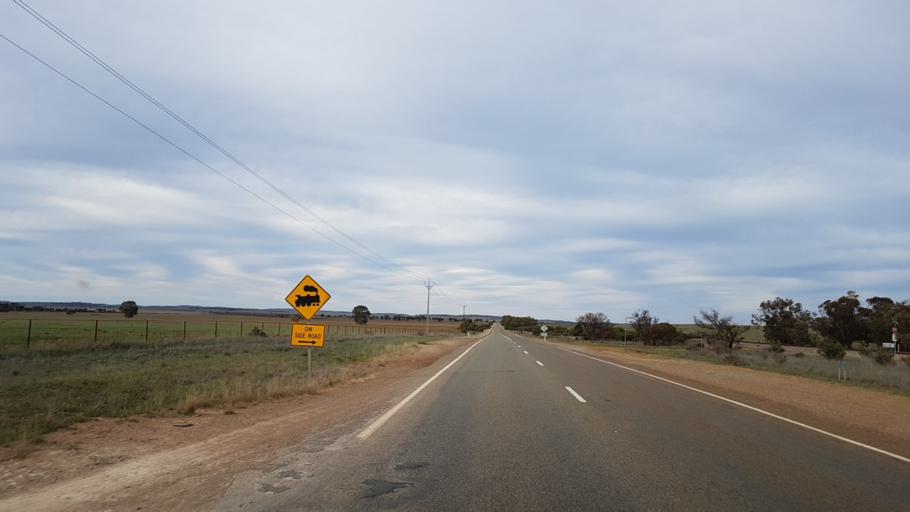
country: AU
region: South Australia
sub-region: Peterborough
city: Peterborough
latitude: -33.0013
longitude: 138.7769
